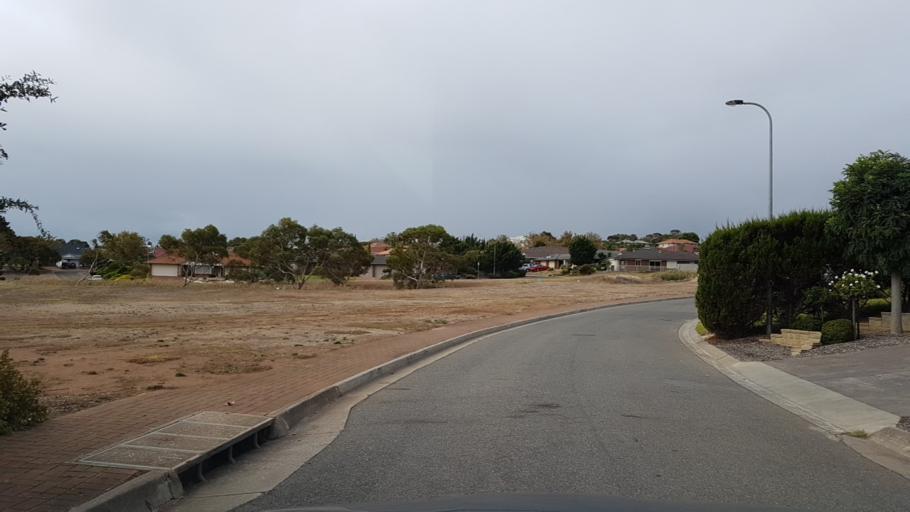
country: AU
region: South Australia
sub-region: Onkaparinga
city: Moana
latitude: -35.2068
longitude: 138.4860
